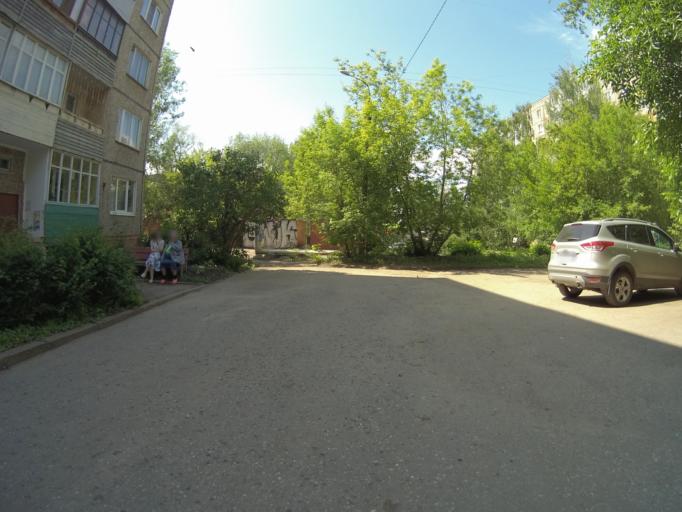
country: RU
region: Vladimir
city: Vladimir
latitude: 56.1295
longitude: 40.3501
